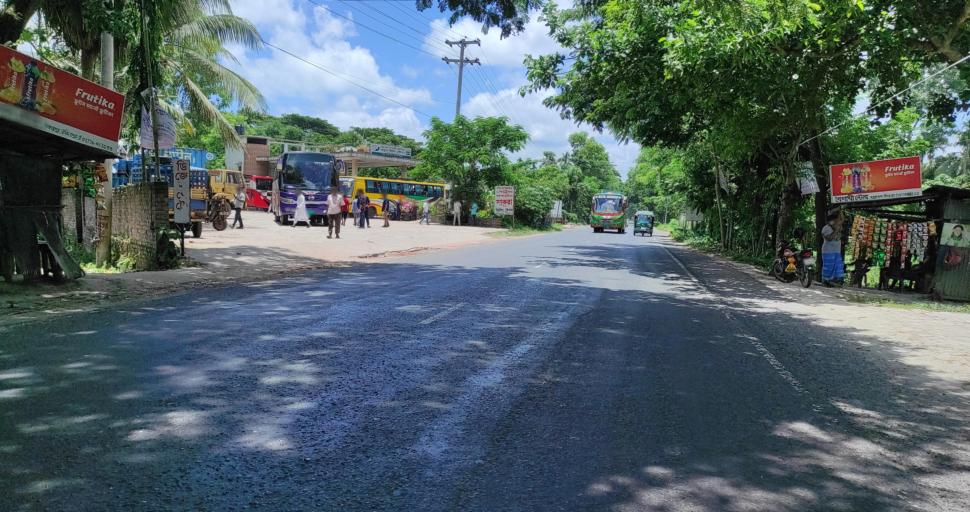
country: BD
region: Barisal
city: Gaurnadi
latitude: 22.8371
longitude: 90.2526
